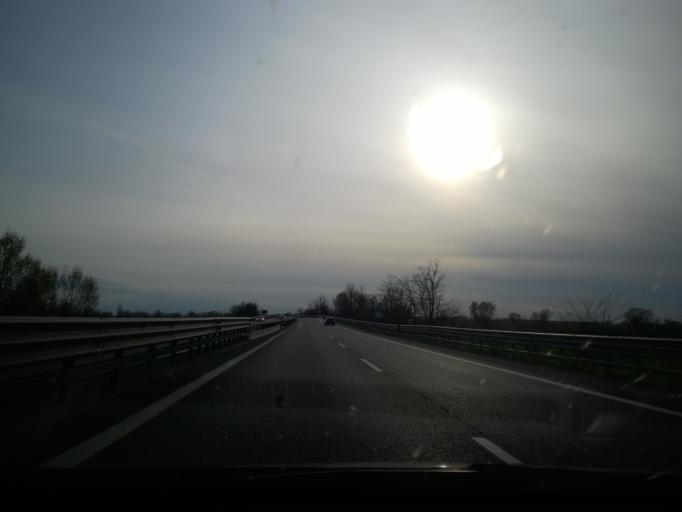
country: IT
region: Lombardy
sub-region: Provincia di Cremona
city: Bosco Ex Parmigiano
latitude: 45.1050
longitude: 10.0333
